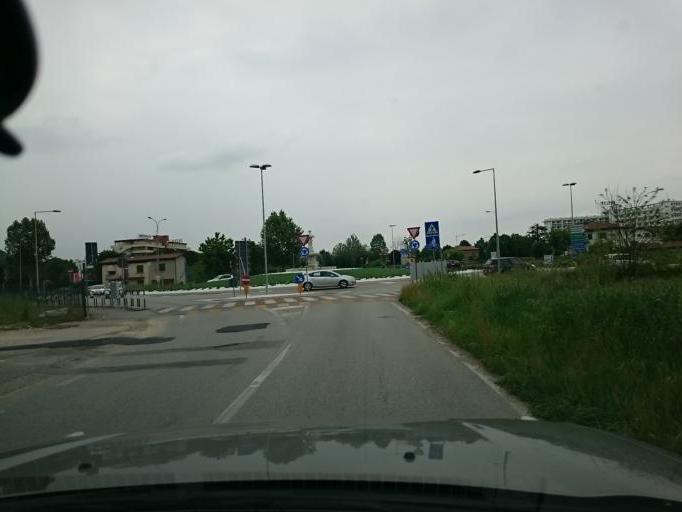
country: IT
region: Veneto
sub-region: Provincia di Padova
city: Montegrotto Terme
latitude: 45.3203
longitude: 11.7858
